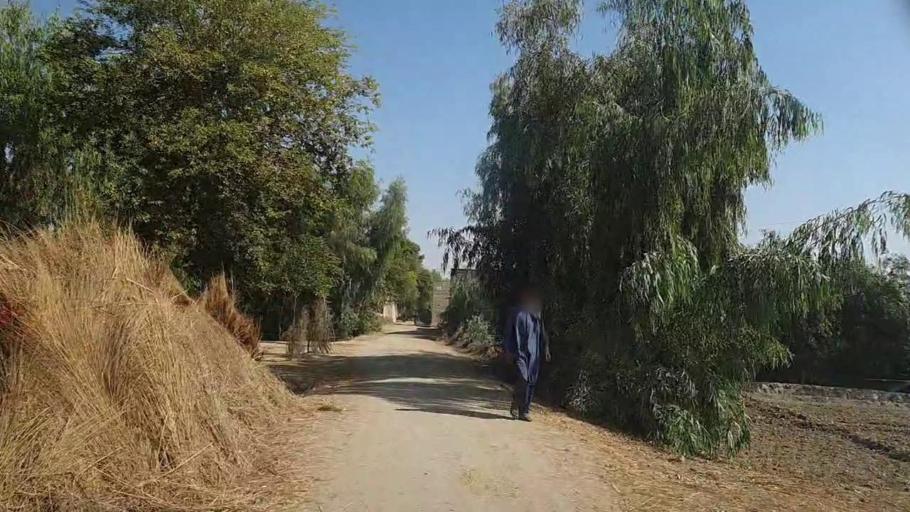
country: PK
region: Sindh
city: Thul
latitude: 28.2565
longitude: 68.8235
